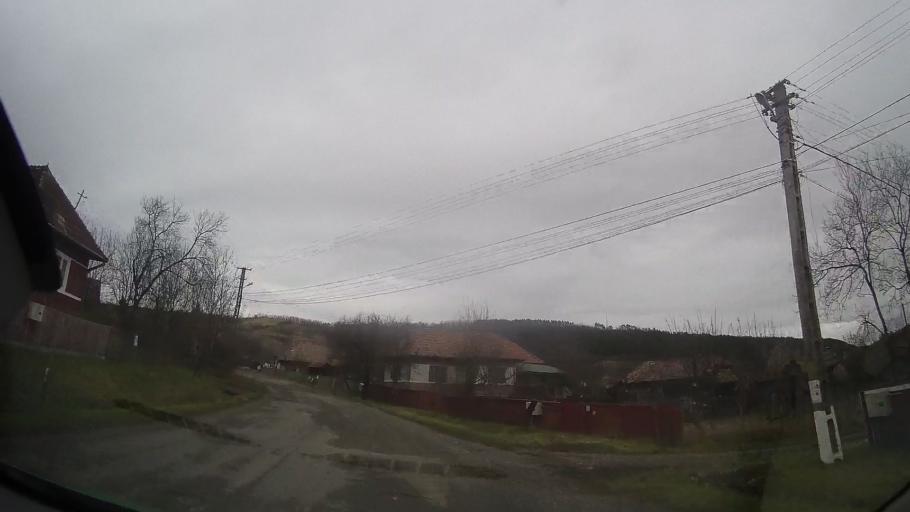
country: RO
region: Mures
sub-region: Comuna Bala
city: Bala
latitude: 46.7115
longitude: 24.5020
